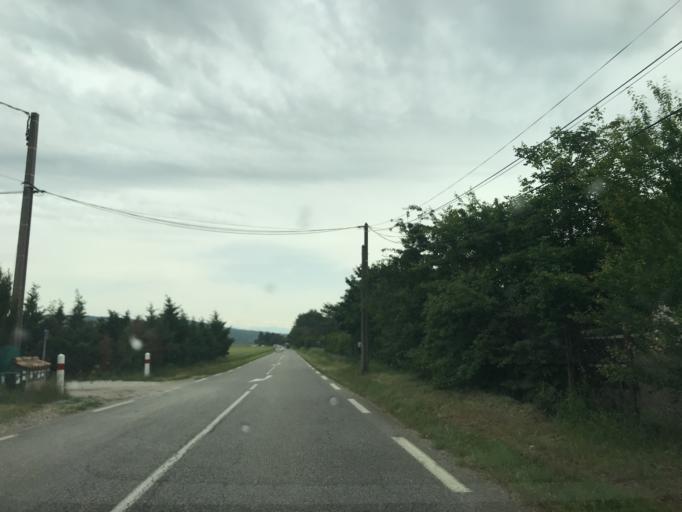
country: FR
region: Provence-Alpes-Cote d'Azur
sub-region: Departement du Var
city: Rians
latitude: 43.6305
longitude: 5.7739
